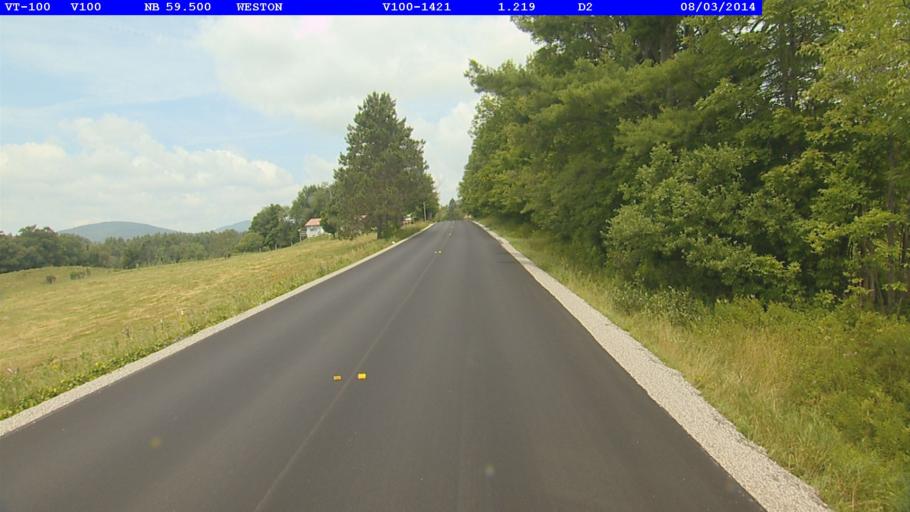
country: US
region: Vermont
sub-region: Windsor County
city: Chester
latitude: 43.2642
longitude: -72.7874
